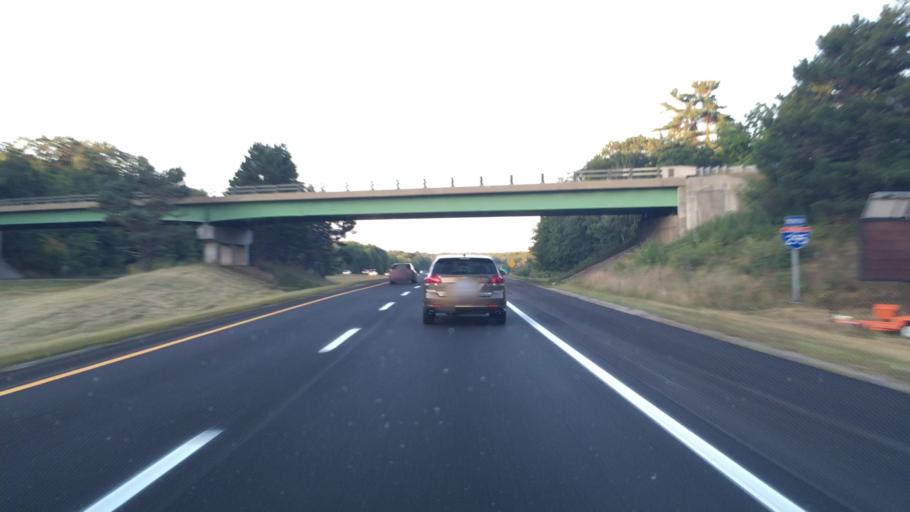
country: US
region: Maine
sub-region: Sagadahoc County
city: Topsham
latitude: 43.9481
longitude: -69.9725
